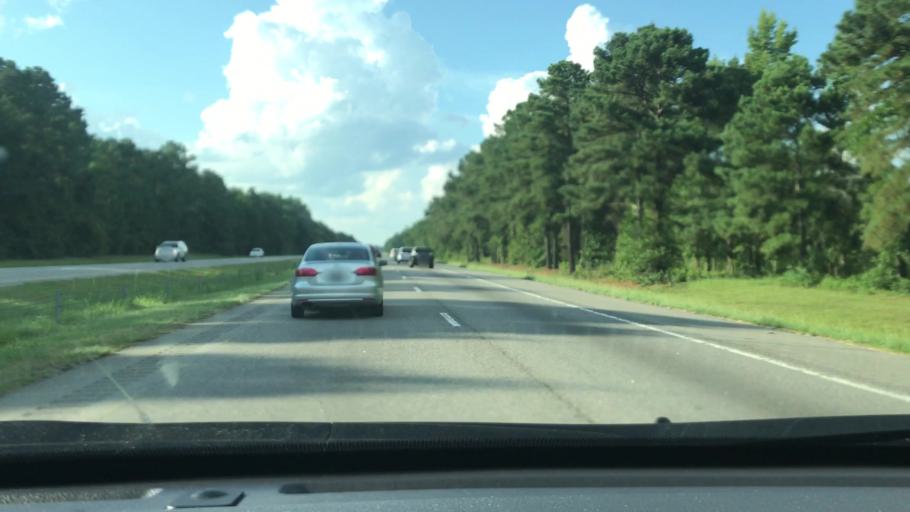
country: US
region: North Carolina
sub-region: Robeson County
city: Saint Pauls
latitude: 34.7402
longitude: -78.9971
